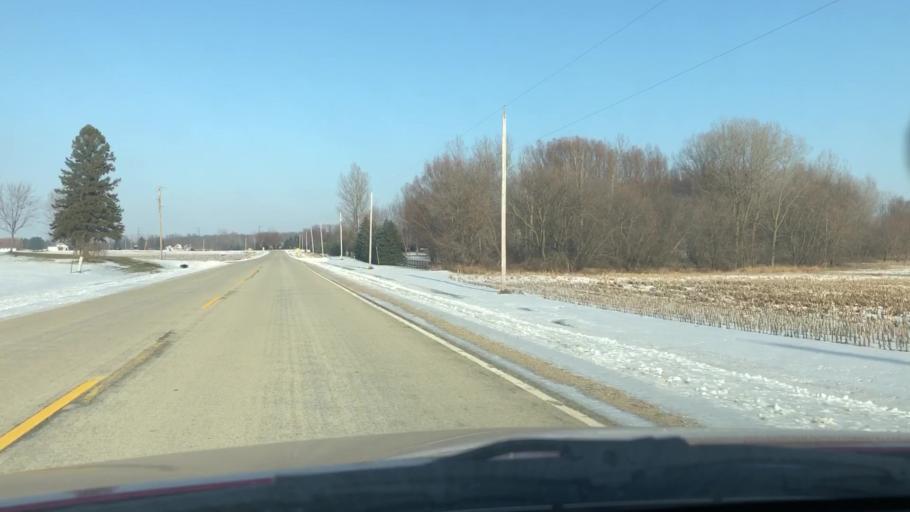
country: US
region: Wisconsin
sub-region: Outagamie County
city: Seymour
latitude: 44.4251
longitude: -88.3657
